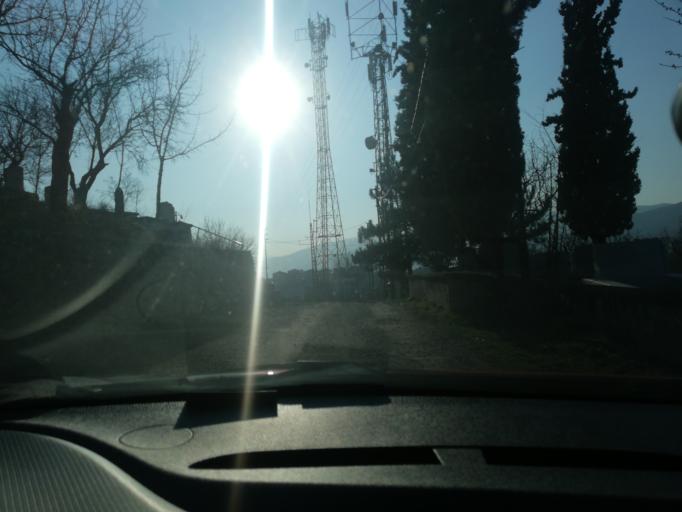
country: TR
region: Karabuk
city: Safranbolu
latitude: 41.2408
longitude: 32.6919
